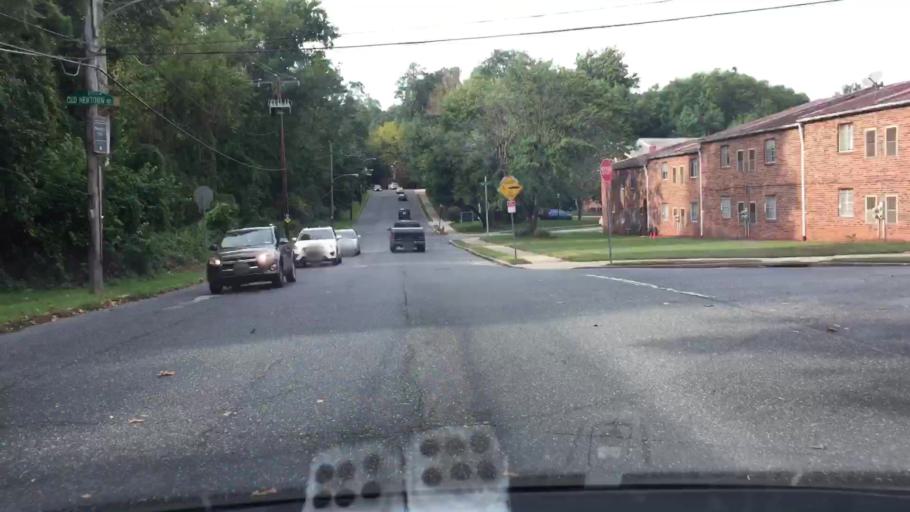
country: US
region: Pennsylvania
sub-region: Montgomery County
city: Rockledge
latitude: 40.0753
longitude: -75.0417
